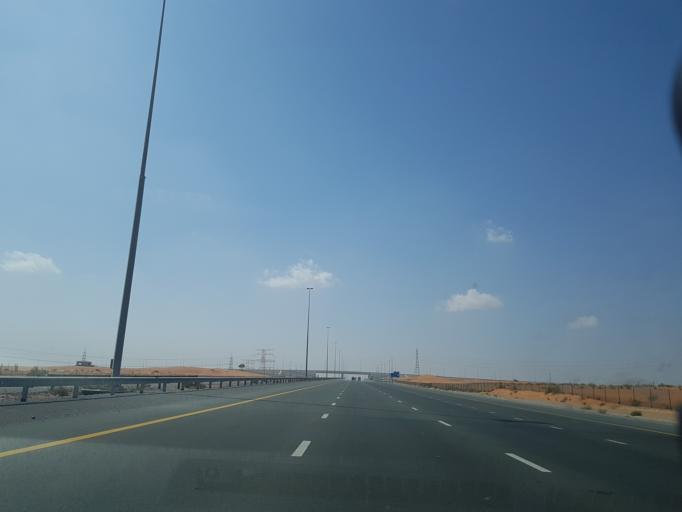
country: AE
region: Ra's al Khaymah
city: Ras al-Khaimah
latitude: 25.6992
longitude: 55.9303
